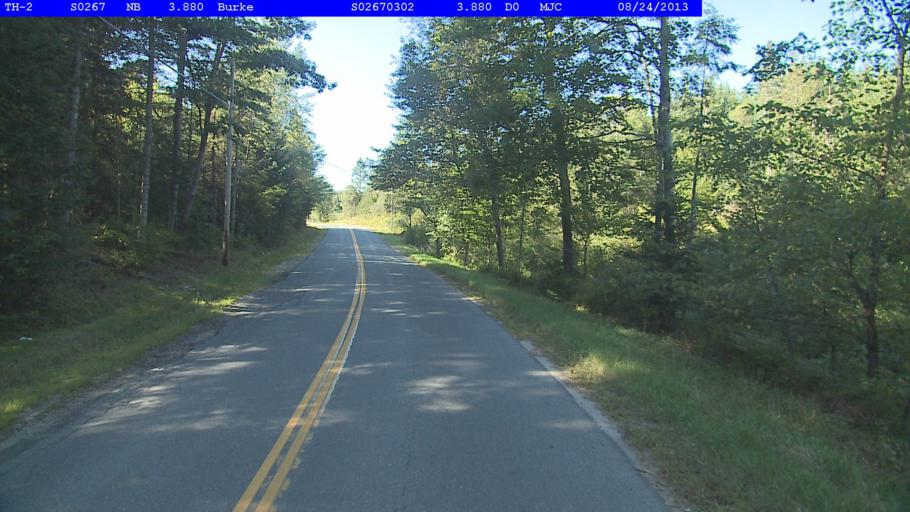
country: US
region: Vermont
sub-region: Caledonia County
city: Lyndonville
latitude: 44.6311
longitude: -71.9656
